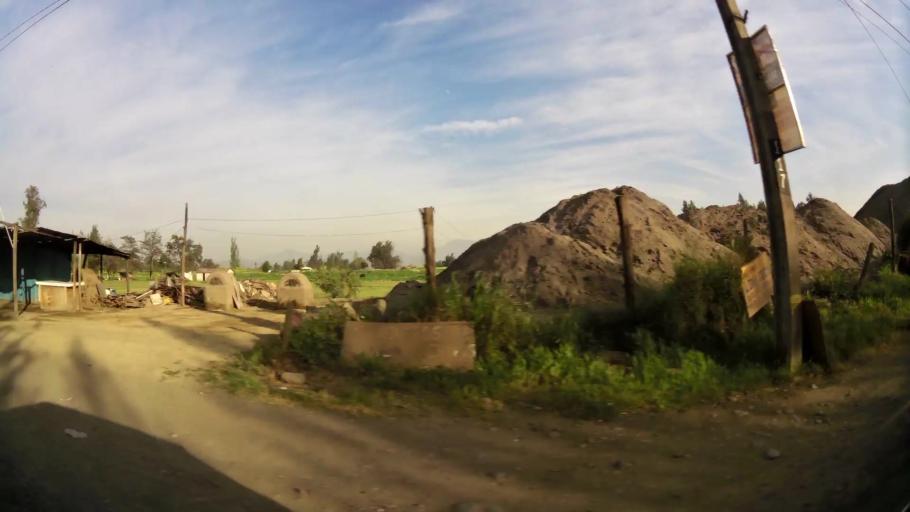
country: CL
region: Santiago Metropolitan
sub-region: Provincia de Maipo
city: San Bernardo
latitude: -33.5530
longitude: -70.7516
